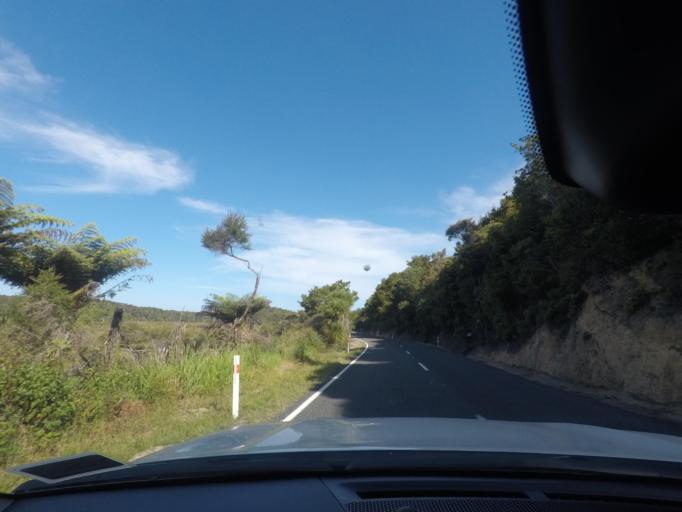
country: NZ
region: Northland
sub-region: Whangarei
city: Ngunguru
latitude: -35.6641
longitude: 174.4825
